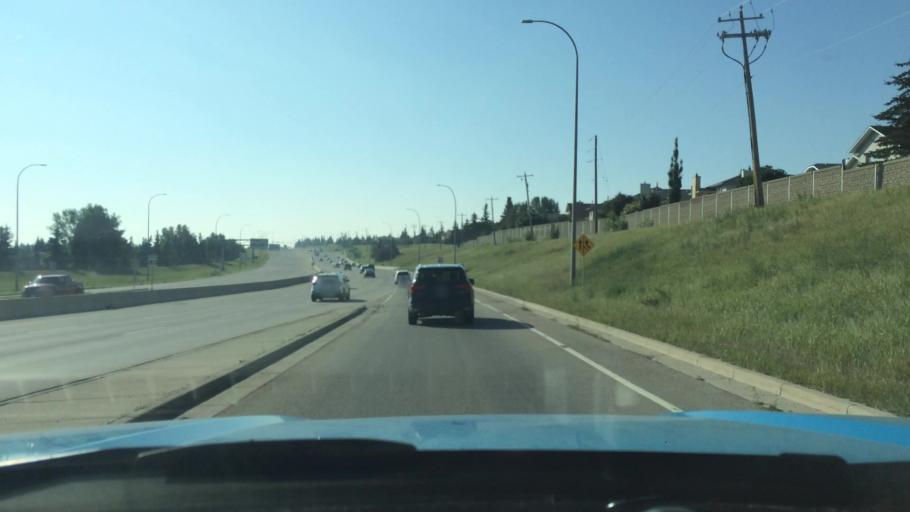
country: CA
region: Alberta
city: Calgary
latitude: 51.1416
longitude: -114.0902
